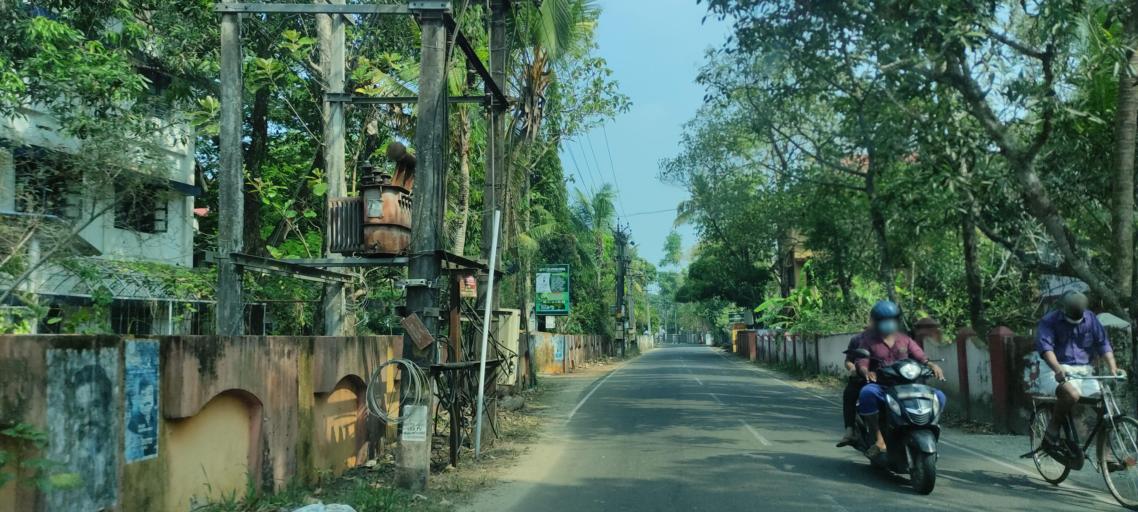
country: IN
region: Kerala
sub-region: Alappuzha
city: Kutiatodu
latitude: 9.7959
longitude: 76.3022
